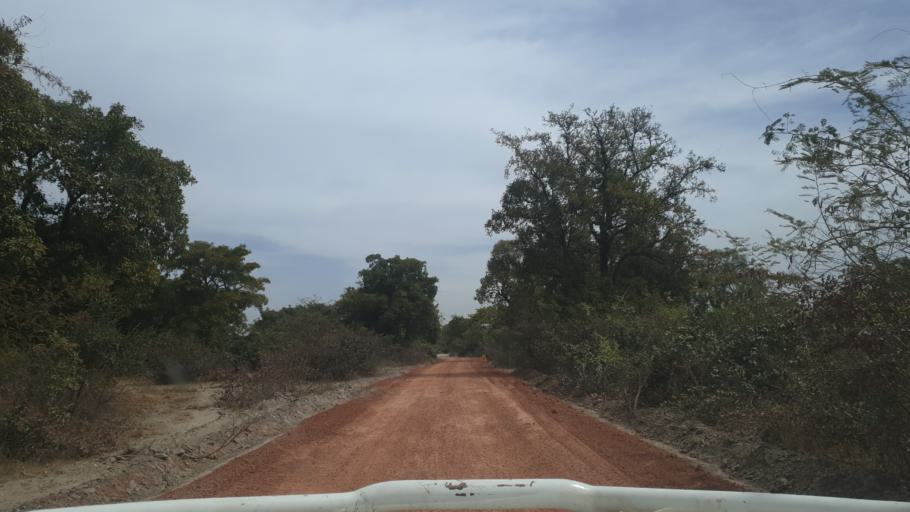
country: ML
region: Sikasso
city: Yorosso
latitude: 12.2358
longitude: -4.7435
